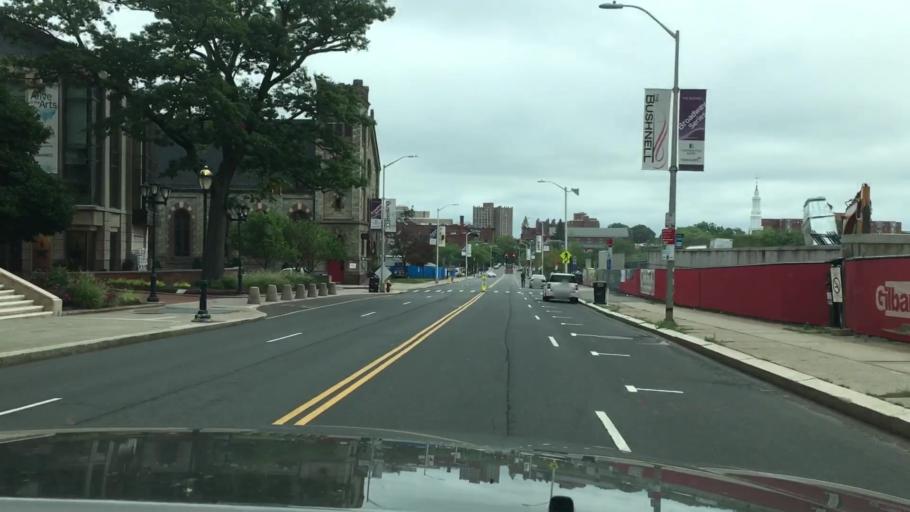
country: US
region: Connecticut
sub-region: Hartford County
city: Hartford
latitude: 41.7624
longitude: -72.6808
